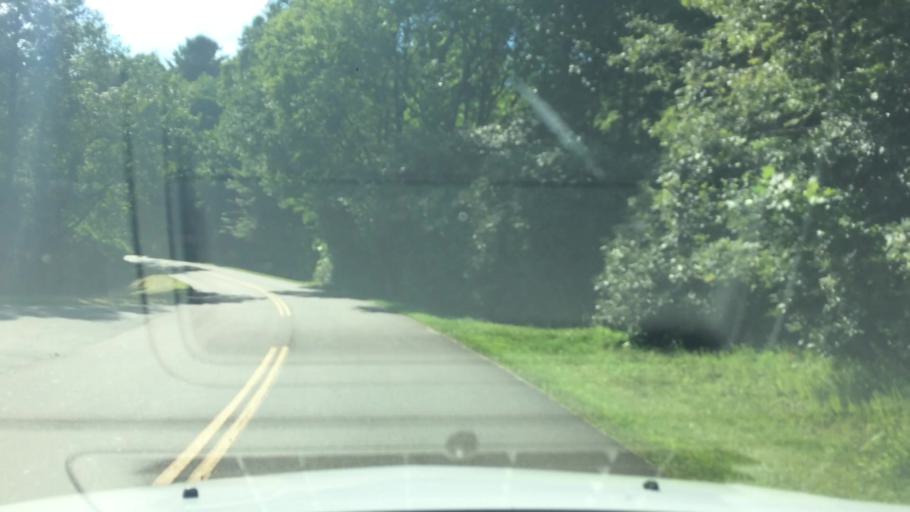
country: US
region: North Carolina
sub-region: Watauga County
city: Foscoe
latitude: 36.1395
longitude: -81.7326
